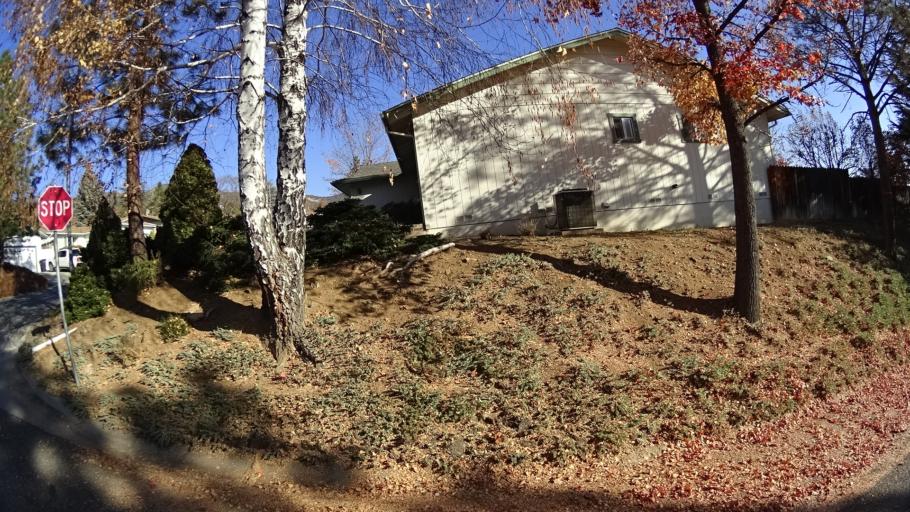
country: US
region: California
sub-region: Siskiyou County
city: Yreka
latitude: 41.7412
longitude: -122.6510
